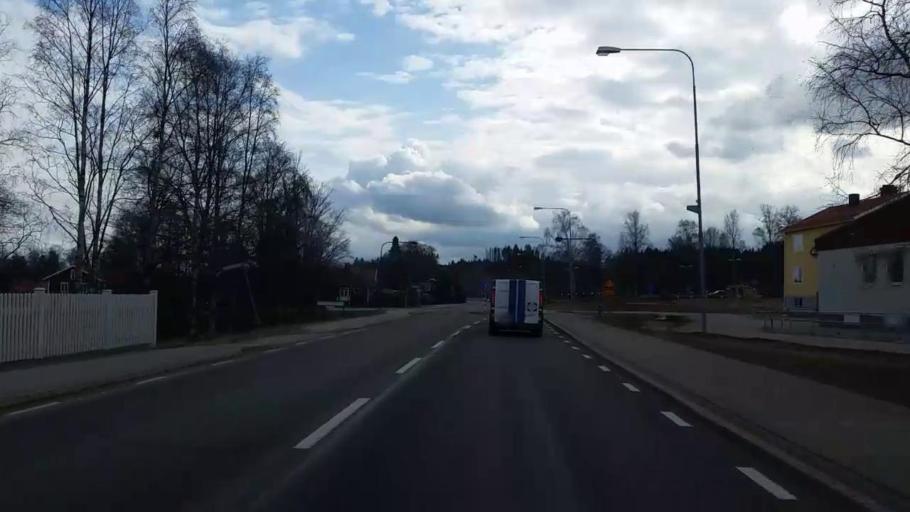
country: SE
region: Gaevleborg
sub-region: Ljusdals Kommun
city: Jaervsoe
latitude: 61.7089
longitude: 16.1641
